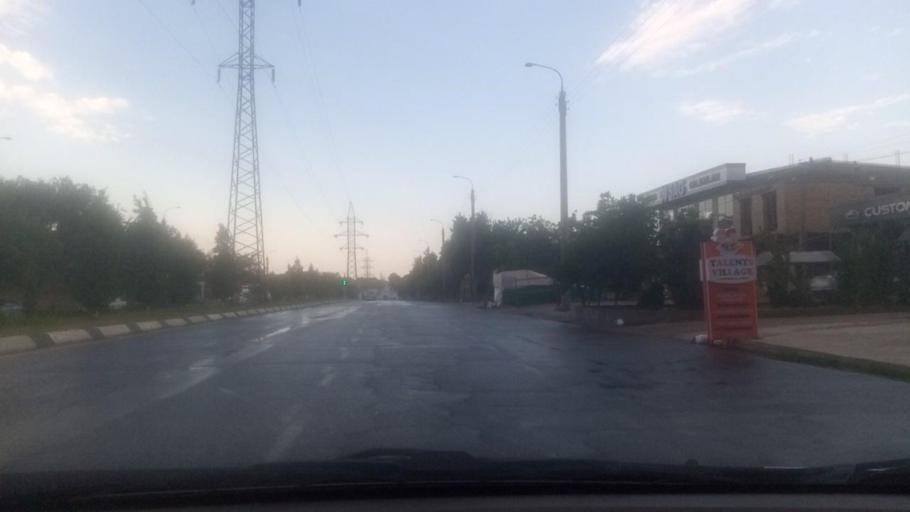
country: UZ
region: Toshkent Shahri
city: Tashkent
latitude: 41.3096
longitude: 69.1934
